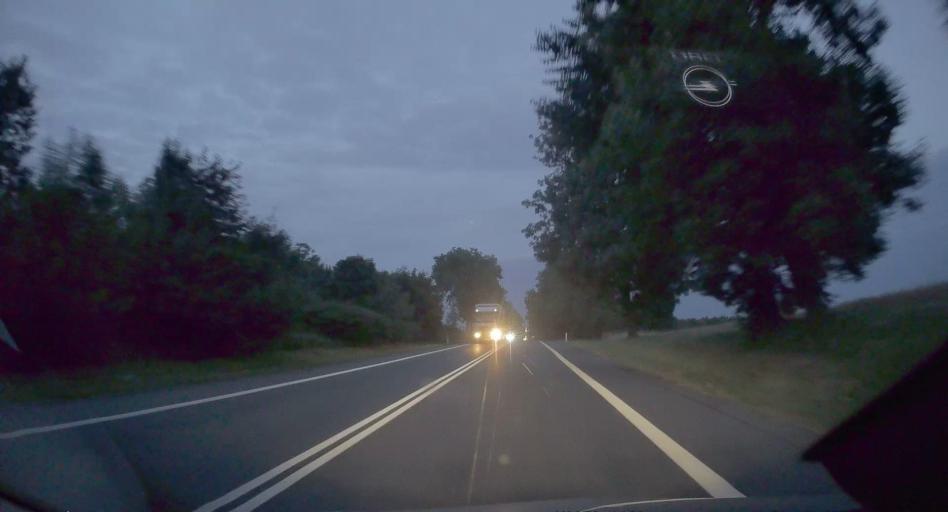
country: PL
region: Silesian Voivodeship
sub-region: Powiat klobucki
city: Klobuck
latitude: 50.9098
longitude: 18.9098
